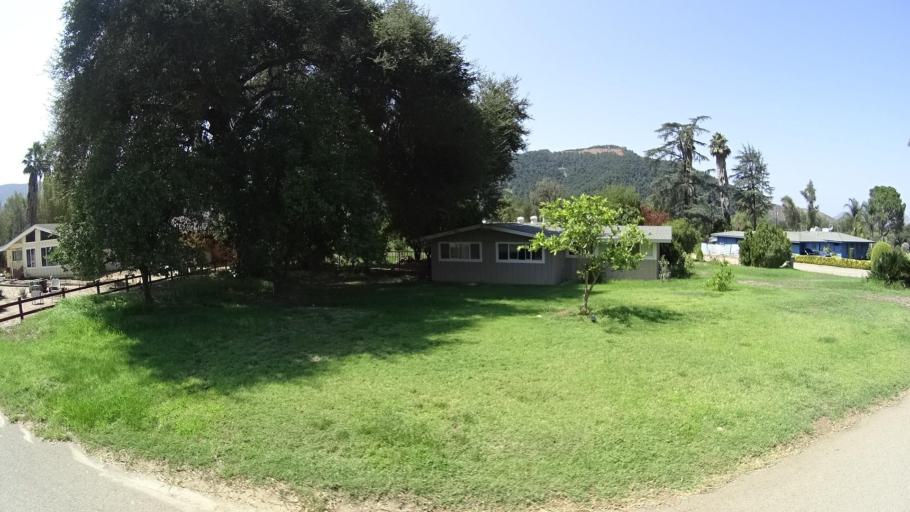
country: US
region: California
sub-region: San Diego County
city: Valley Center
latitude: 33.2902
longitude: -116.9692
